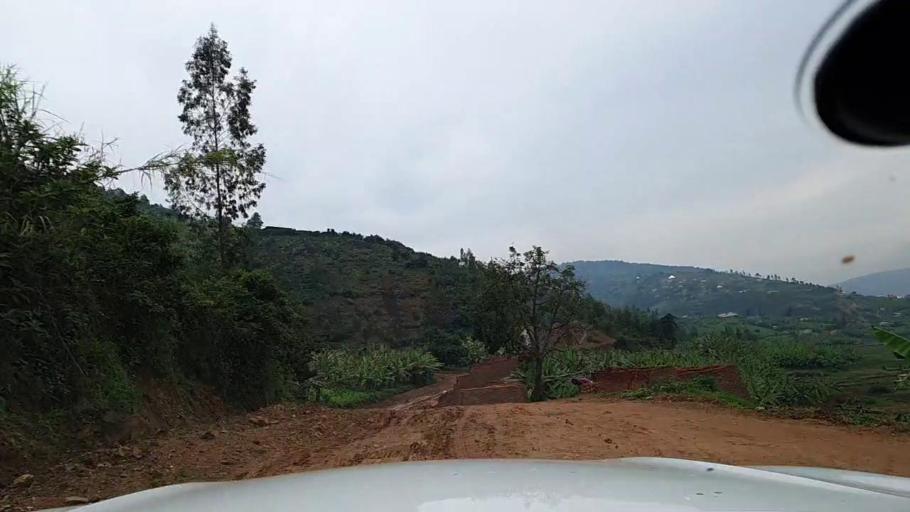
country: RW
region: Kigali
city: Kigali
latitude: -1.9529
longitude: 29.9918
